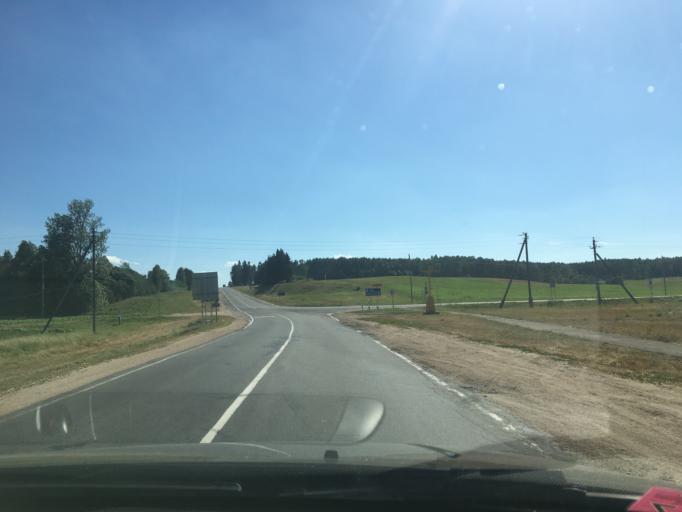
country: BY
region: Grodnenskaya
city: Hal'shany
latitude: 54.2542
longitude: 26.0077
